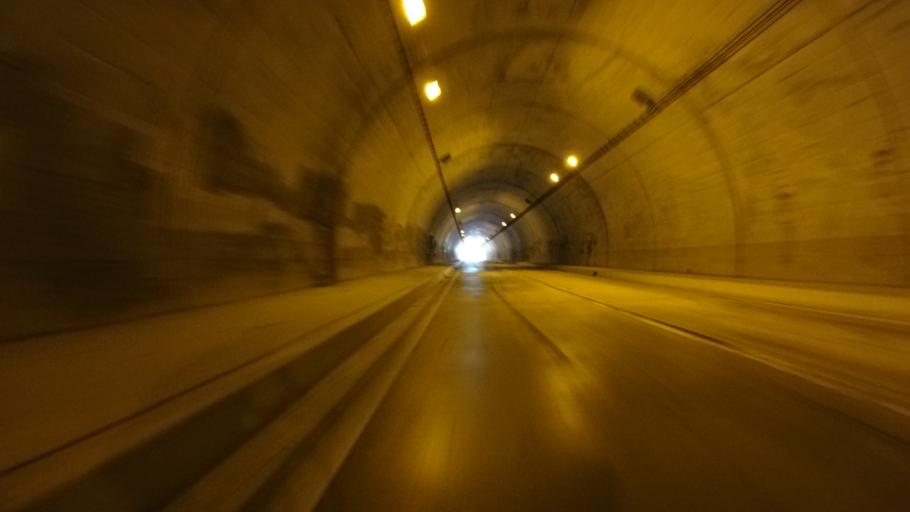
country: JP
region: Kanagawa
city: Hadano
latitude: 35.5124
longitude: 139.2314
